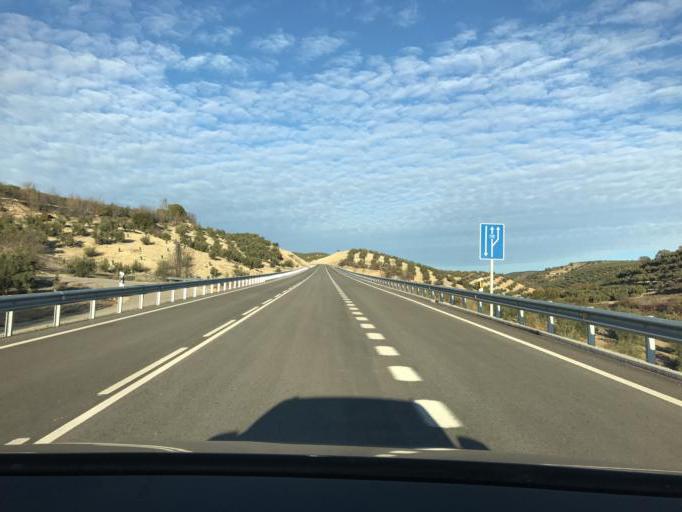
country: ES
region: Andalusia
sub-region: Provincia de Granada
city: Pinar
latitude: 37.4553
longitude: -3.4751
